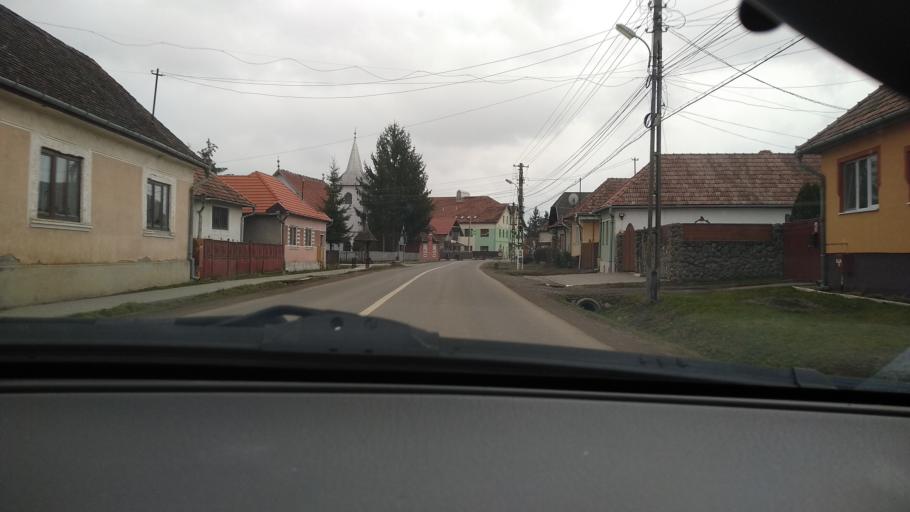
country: RO
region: Mures
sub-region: Comuna Miercurea Nirajului
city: Miercurea Nirajului
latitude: 46.5391
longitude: 24.8186
